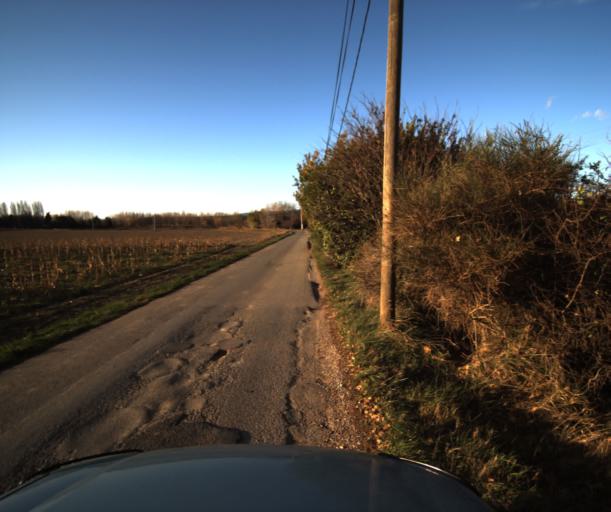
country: FR
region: Provence-Alpes-Cote d'Azur
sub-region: Departement du Vaucluse
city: Pertuis
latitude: 43.6730
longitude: 5.5279
